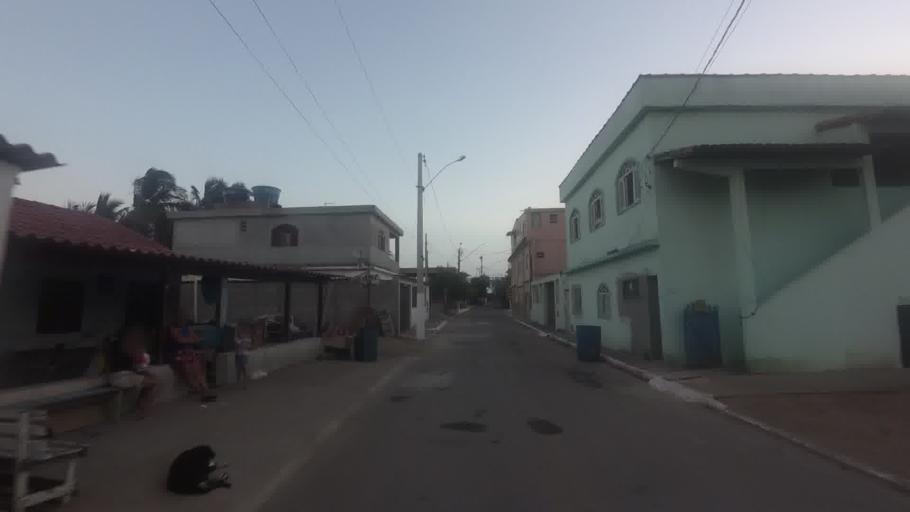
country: BR
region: Espirito Santo
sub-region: Piuma
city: Piuma
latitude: -20.8910
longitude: -40.7672
